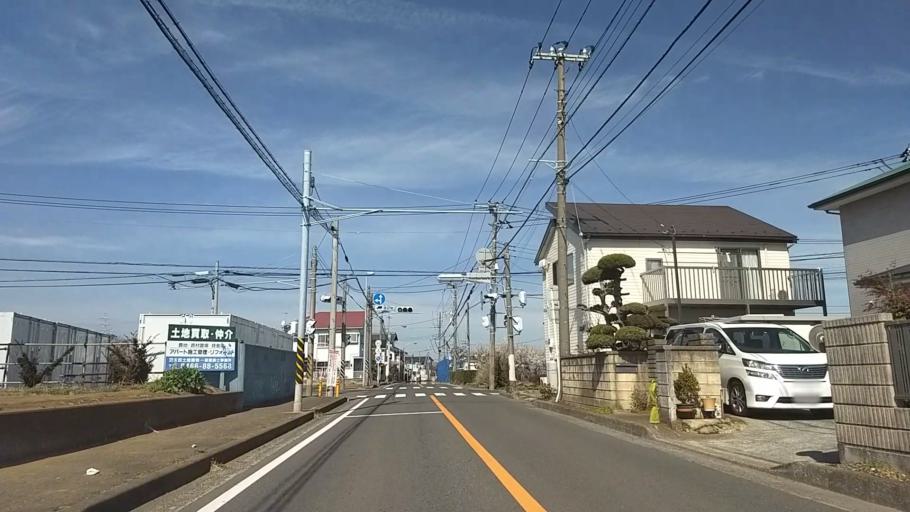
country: JP
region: Kanagawa
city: Fujisawa
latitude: 35.3817
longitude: 139.4376
